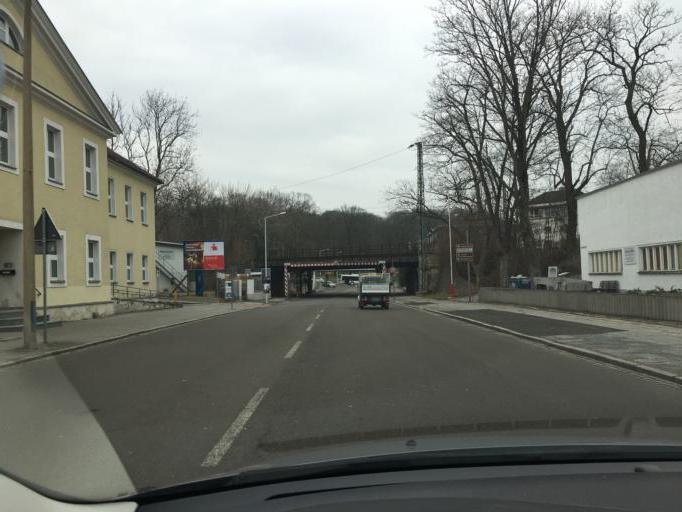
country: DE
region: Thuringia
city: Altenburg
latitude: 50.9946
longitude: 12.4466
